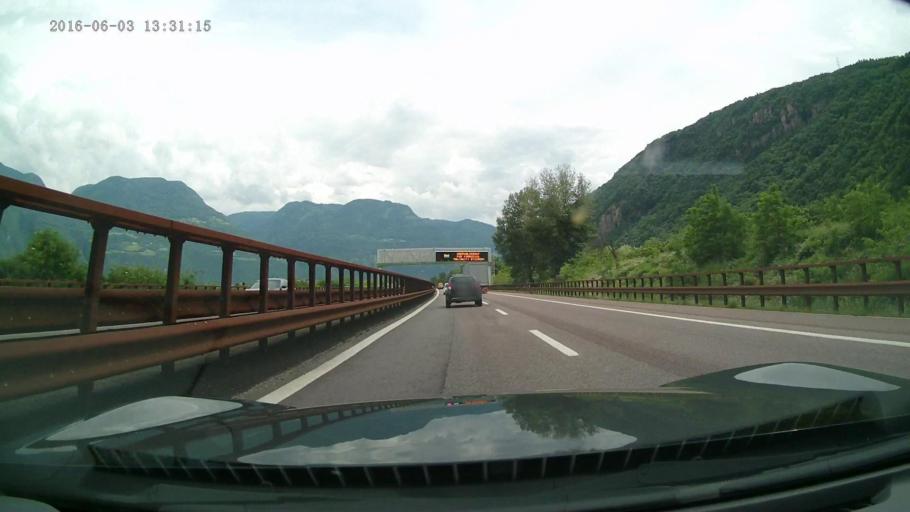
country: IT
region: Trentino-Alto Adige
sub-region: Bolzano
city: Cornaiano
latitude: 46.4537
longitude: 11.3059
